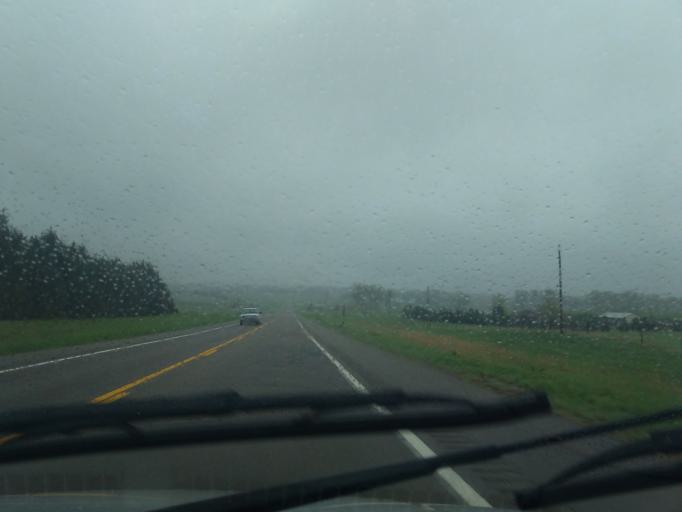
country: US
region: Nebraska
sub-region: Madison County
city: Norfolk
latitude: 42.0898
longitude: -97.3215
